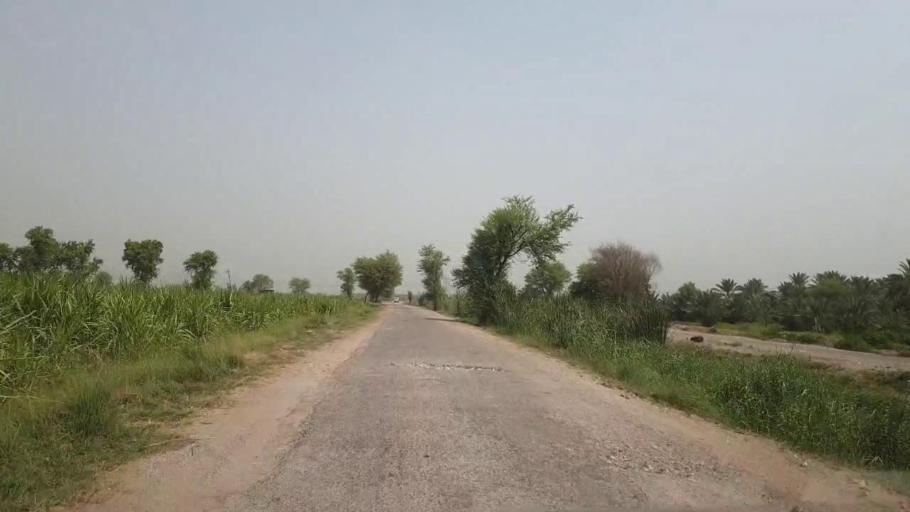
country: PK
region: Sindh
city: Gambat
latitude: 27.4068
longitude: 68.5505
